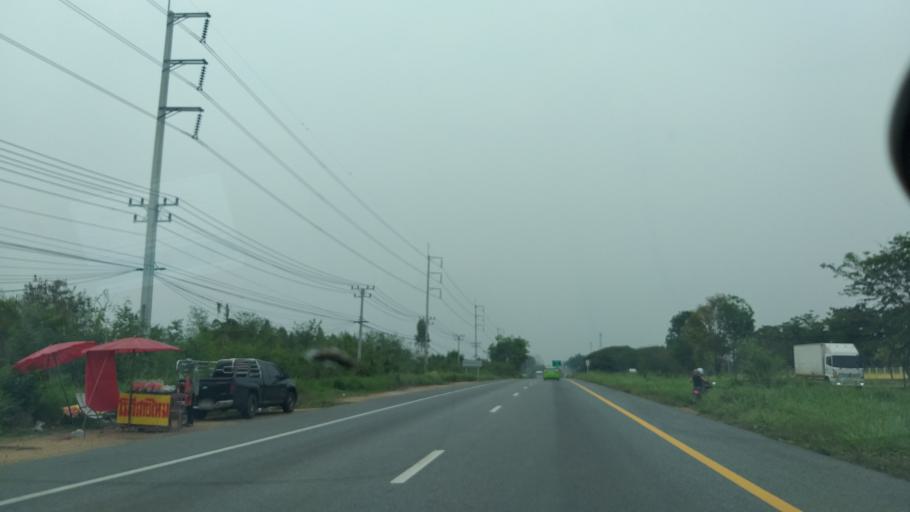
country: TH
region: Chon Buri
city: Ko Chan
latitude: 13.4210
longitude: 101.2824
